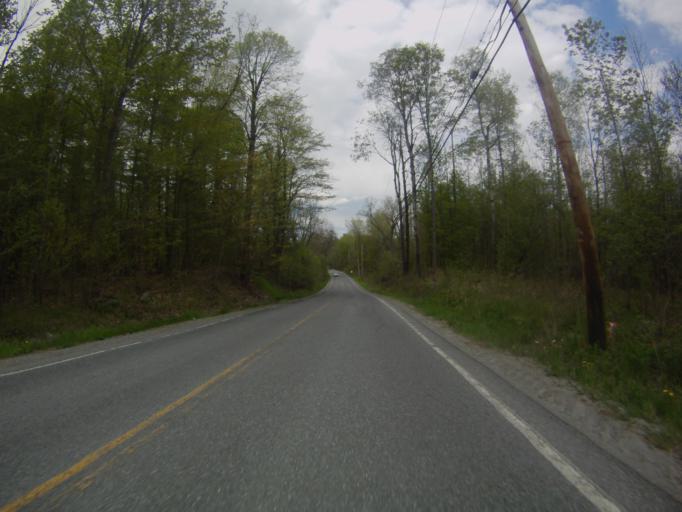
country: US
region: New York
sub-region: Essex County
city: Port Henry
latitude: 44.0177
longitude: -73.4999
